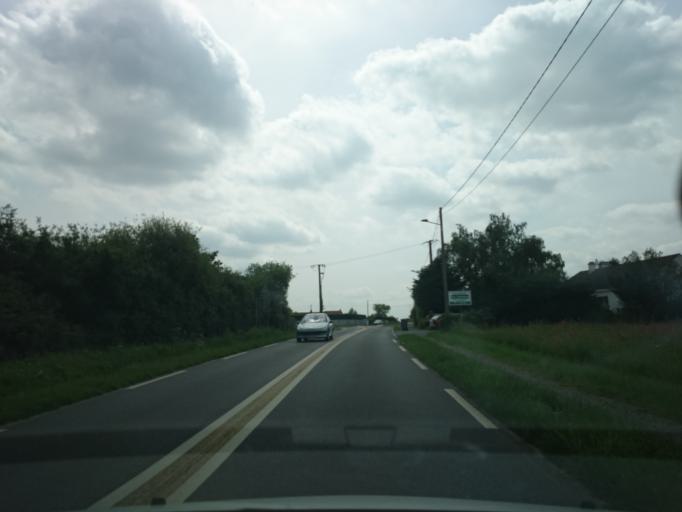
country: FR
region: Pays de la Loire
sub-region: Departement de la Loire-Atlantique
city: Pont-Saint-Martin
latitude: 47.1081
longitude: -1.5882
